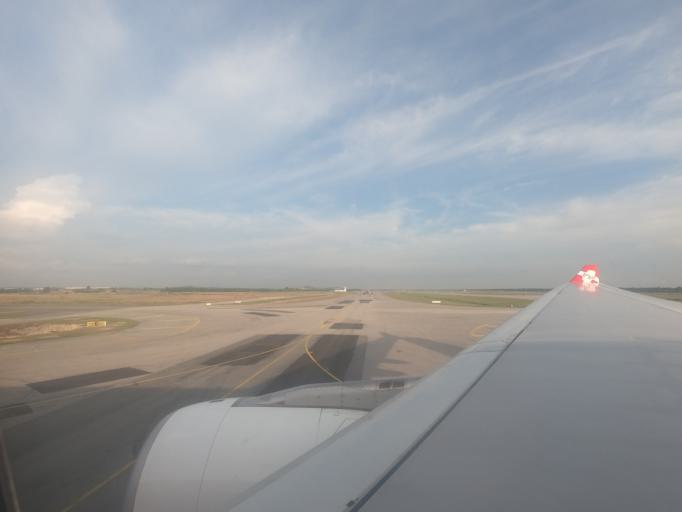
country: MY
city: Sungai Pelek New Village
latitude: 2.7340
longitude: 101.6836
